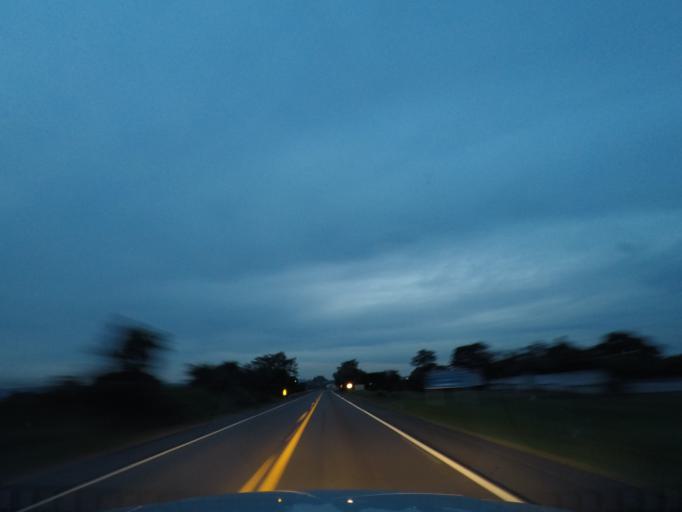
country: BR
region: Bahia
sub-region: Andarai
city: Vera Cruz
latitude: -12.5012
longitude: -41.2864
